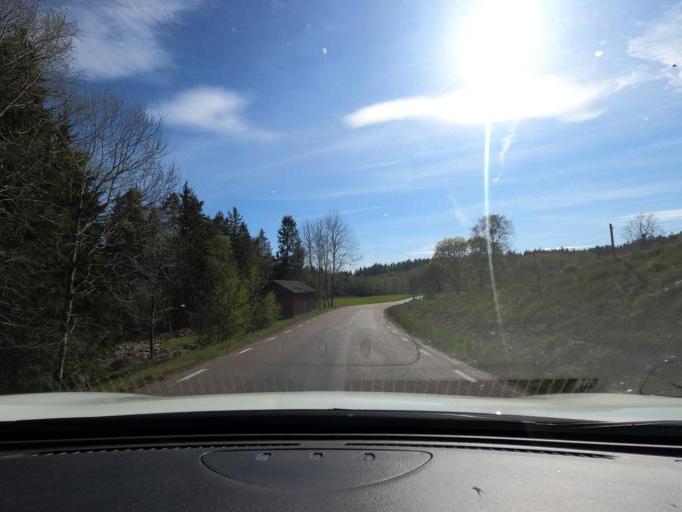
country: SE
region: Vaestra Goetaland
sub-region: Harryda Kommun
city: Hindas
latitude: 57.6405
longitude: 12.3442
